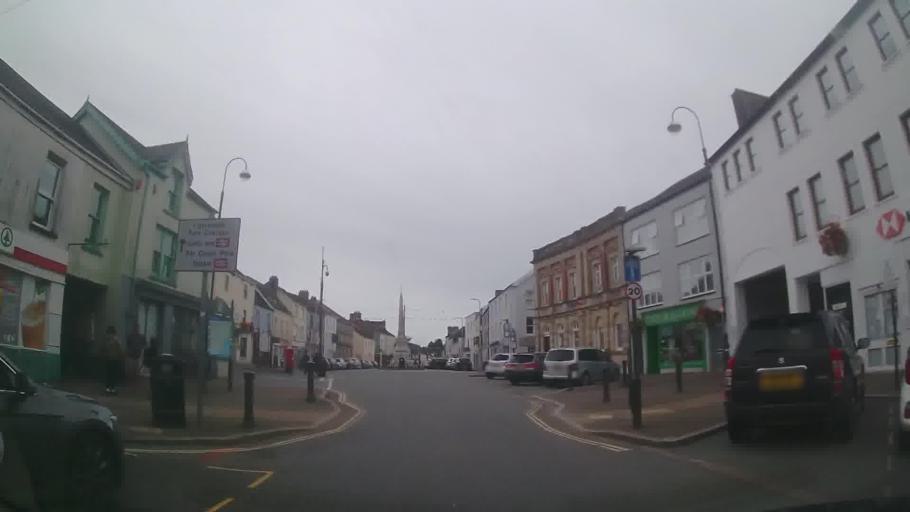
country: GB
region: Wales
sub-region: Carmarthenshire
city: Carmarthen
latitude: 51.8566
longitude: -4.3100
